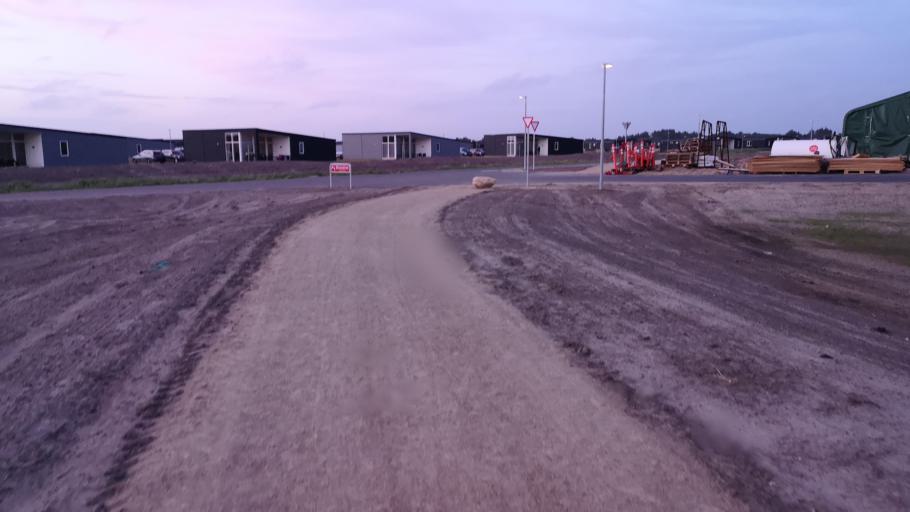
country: DK
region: Central Jutland
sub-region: Ringkobing-Skjern Kommune
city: Hvide Sande
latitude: 56.1214
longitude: 8.1187
